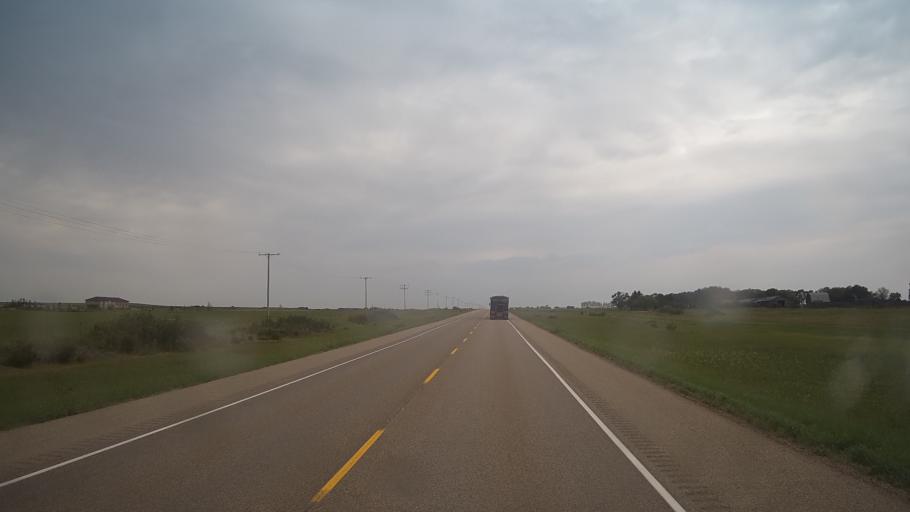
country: CA
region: Saskatchewan
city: Langham
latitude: 52.1289
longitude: -107.1636
